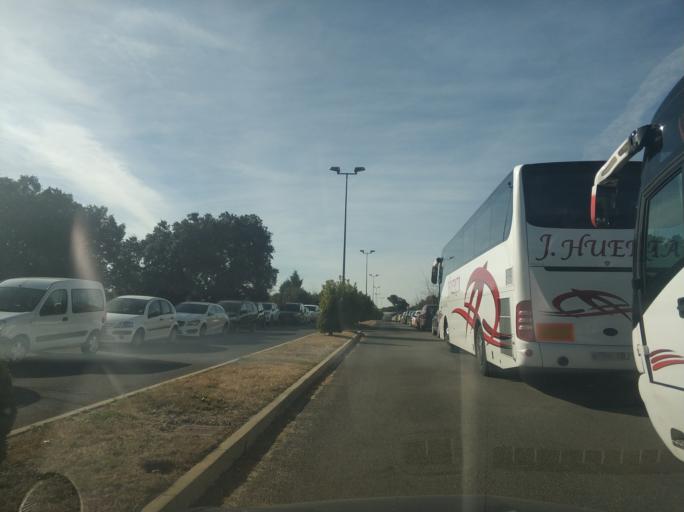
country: ES
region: Castille and Leon
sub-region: Provincia de Salamanca
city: San Pedro del Valle
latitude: 41.0134
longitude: -5.8510
